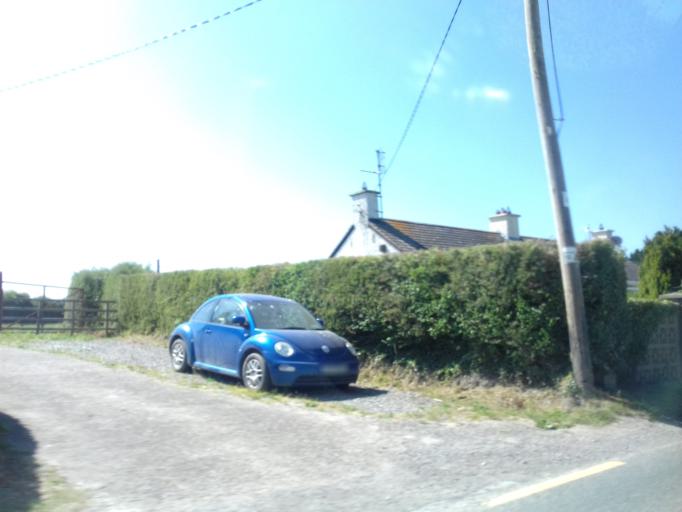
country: IE
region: Leinster
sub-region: An Mhi
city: Stamullin
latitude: 53.5374
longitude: -6.2710
